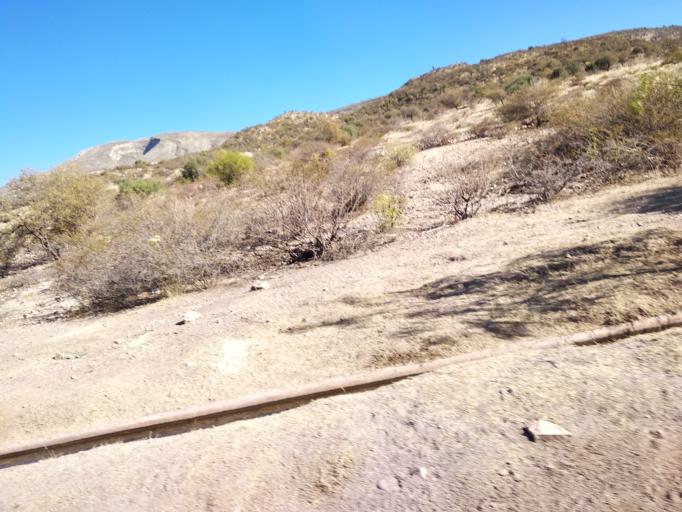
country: BO
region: Cochabamba
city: Mizque
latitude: -18.0807
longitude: -65.7463
